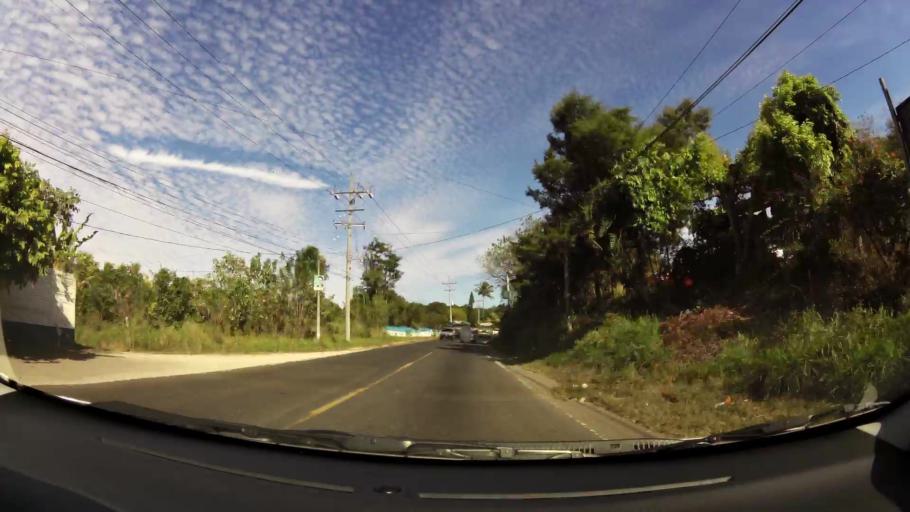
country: SV
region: Santa Ana
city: Santa Ana
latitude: 13.9852
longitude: -89.5950
